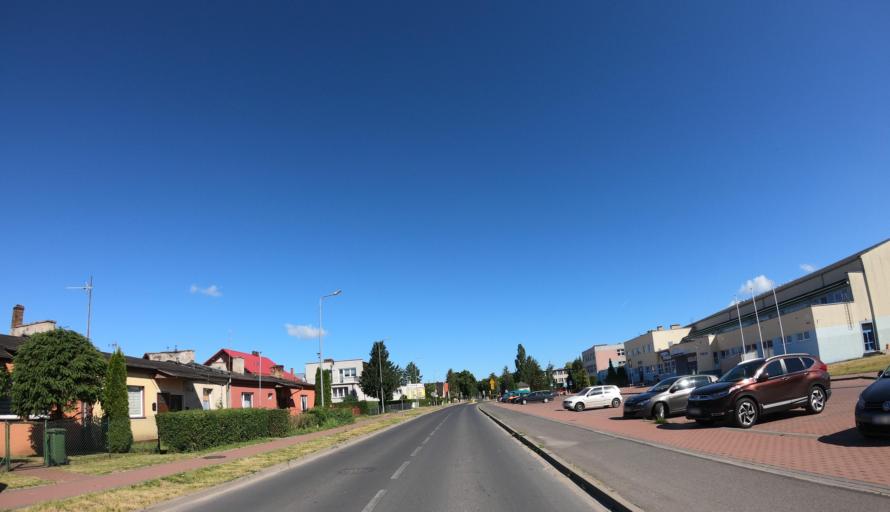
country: PL
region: West Pomeranian Voivodeship
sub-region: Powiat kamienski
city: Kamien Pomorski
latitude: 53.9602
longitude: 14.7764
